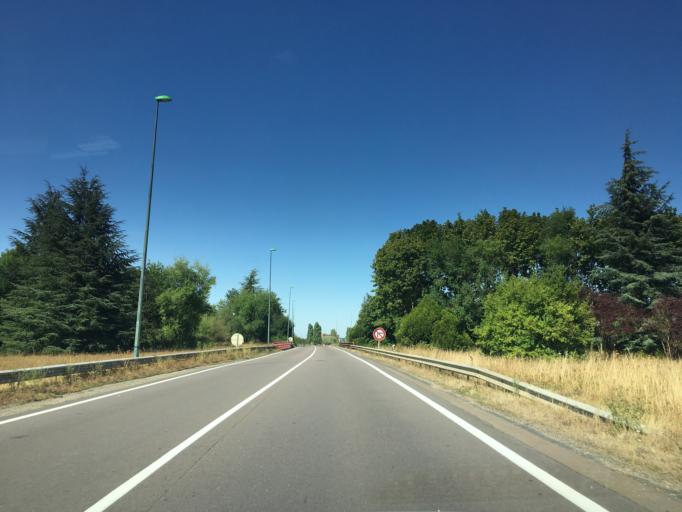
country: FR
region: Bourgogne
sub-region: Departement de l'Yonne
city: Maillot
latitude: 48.1899
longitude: 3.3110
